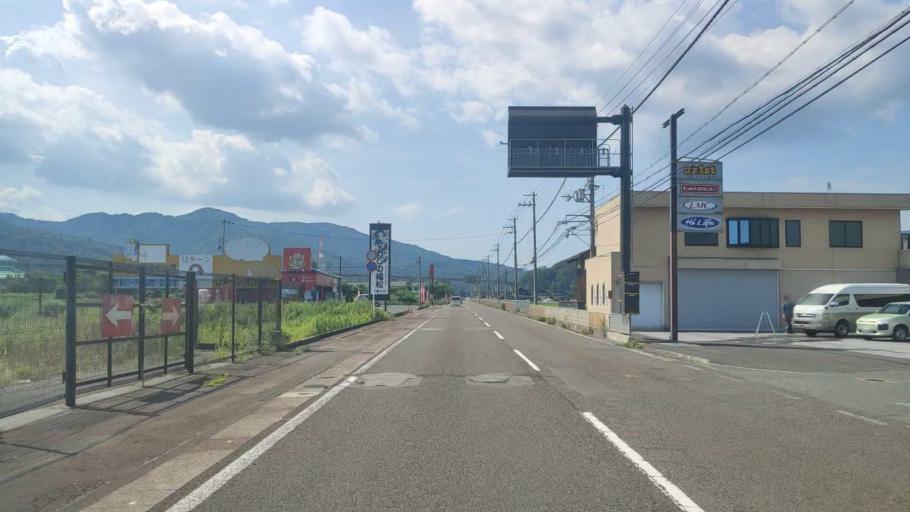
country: JP
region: Fukui
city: Tsuruga
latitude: 35.5252
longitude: 136.1601
